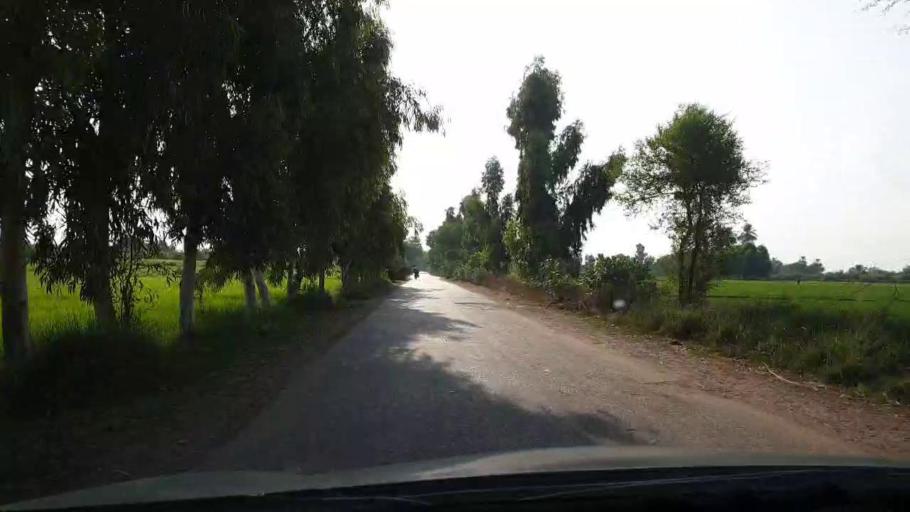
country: PK
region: Sindh
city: Larkana
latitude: 27.5500
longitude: 68.2436
